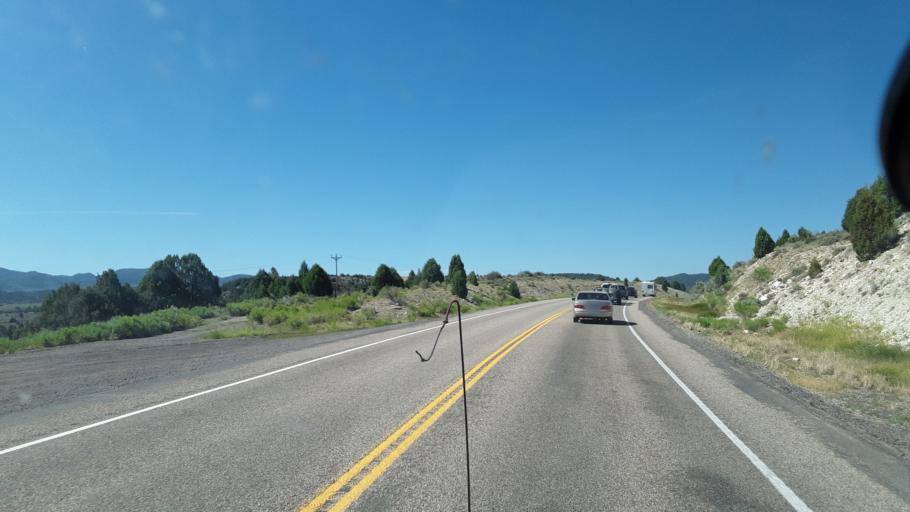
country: US
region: Utah
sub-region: Garfield County
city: Panguitch
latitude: 37.5936
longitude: -112.4724
